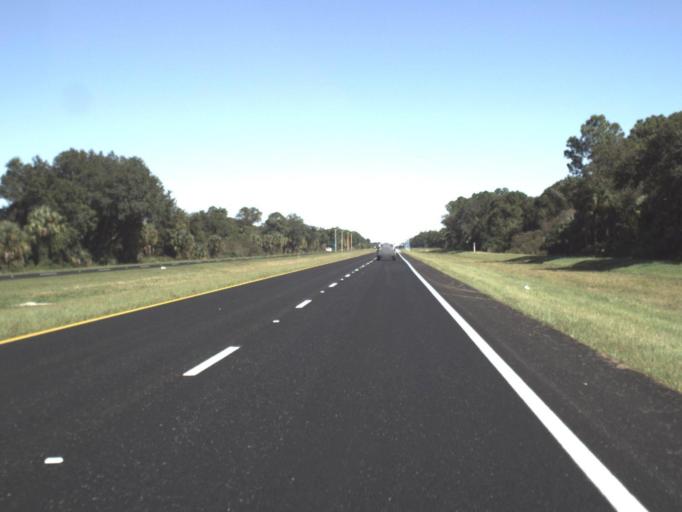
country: US
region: Florida
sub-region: Hendry County
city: Port LaBelle
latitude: 26.7684
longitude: -81.3648
